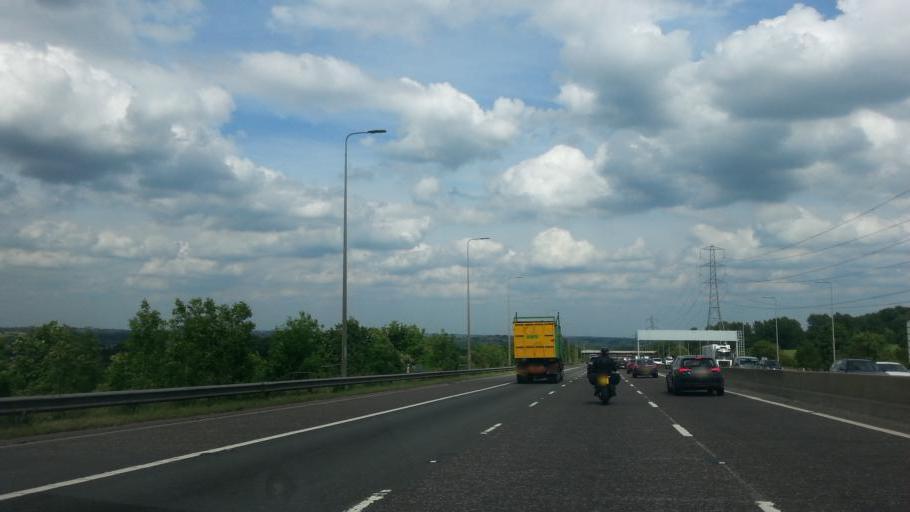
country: GB
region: England
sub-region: Calderdale
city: Brighouse
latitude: 53.6815
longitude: -1.7929
